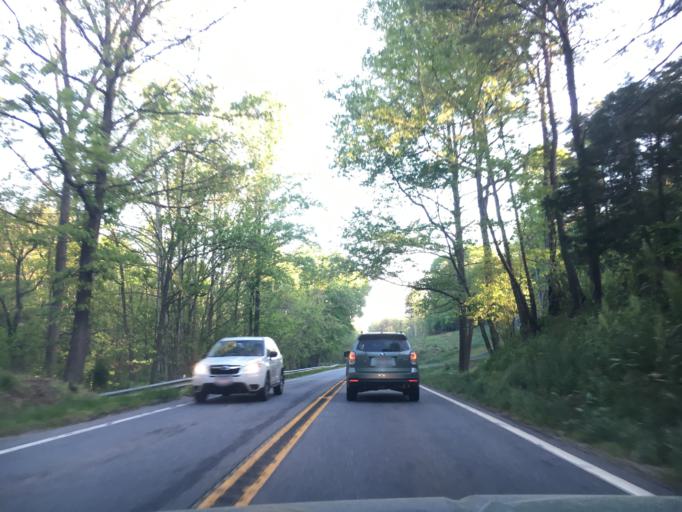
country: US
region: Virginia
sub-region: Campbell County
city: Rustburg
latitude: 37.2906
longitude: -79.1080
